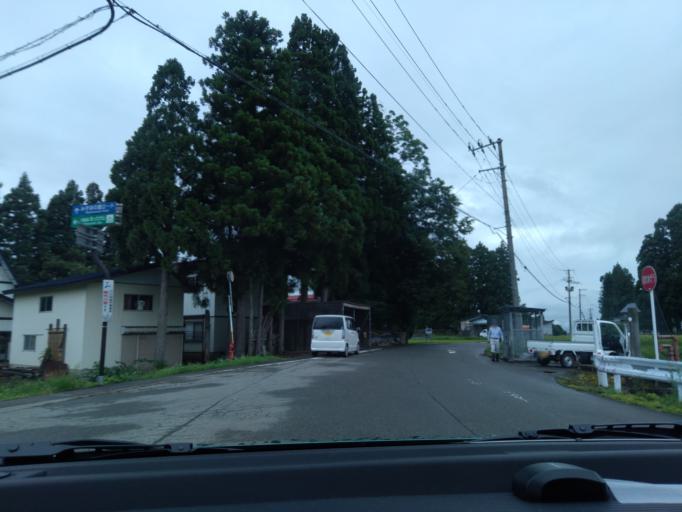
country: JP
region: Akita
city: Yokotemachi
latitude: 39.4182
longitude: 140.5924
